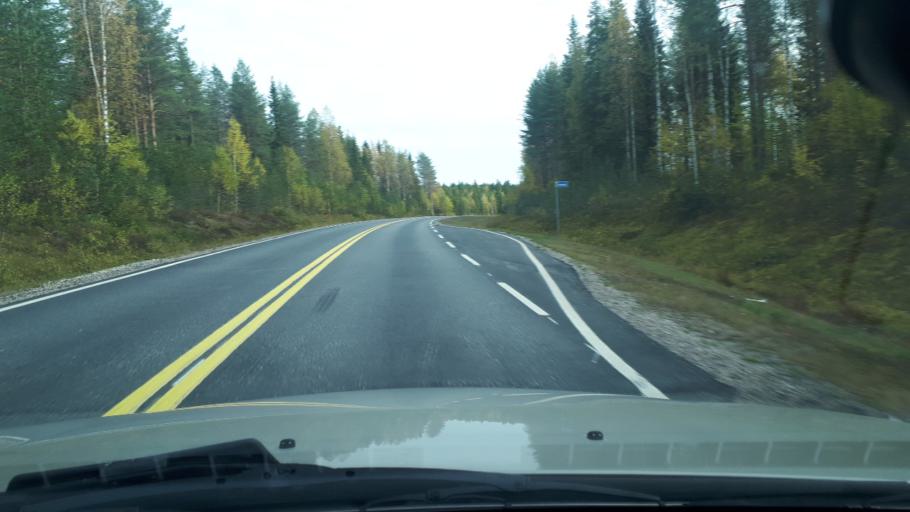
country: FI
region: Lapland
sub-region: Rovaniemi
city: Ranua
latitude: 65.9673
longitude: 26.0016
